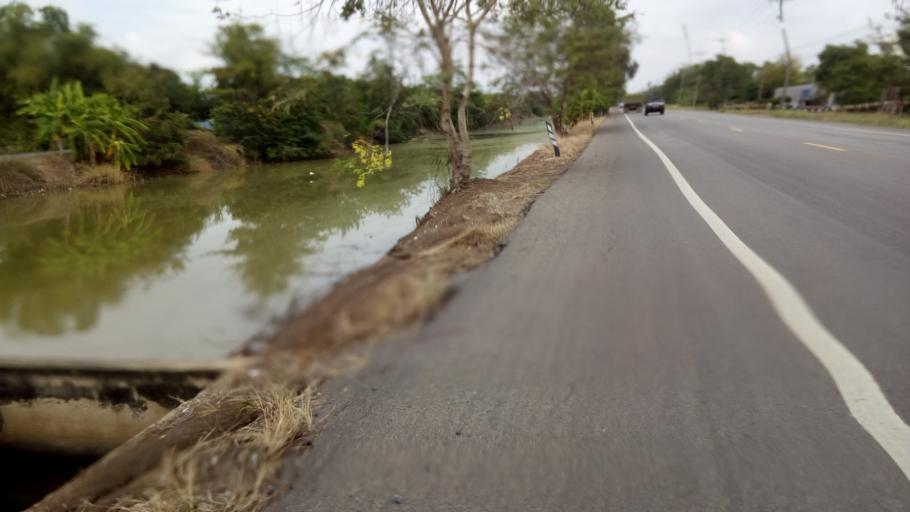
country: TH
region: Pathum Thani
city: Nong Suea
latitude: 14.2200
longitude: 100.8233
